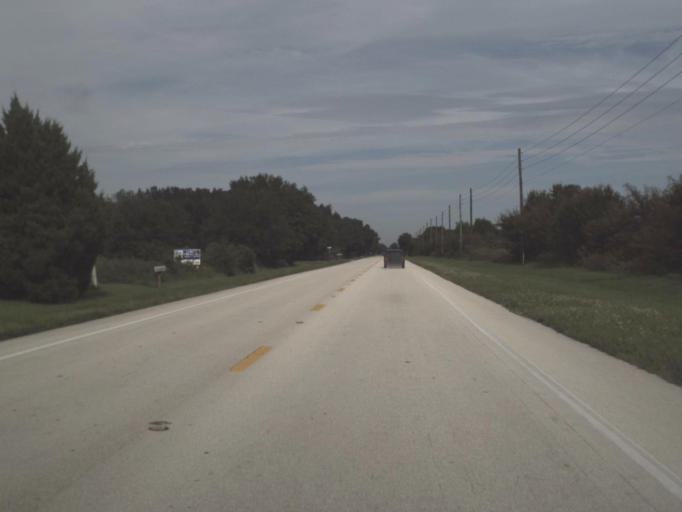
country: US
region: Florida
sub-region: DeSoto County
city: Southeast Arcadia
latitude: 27.1603
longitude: -81.8164
